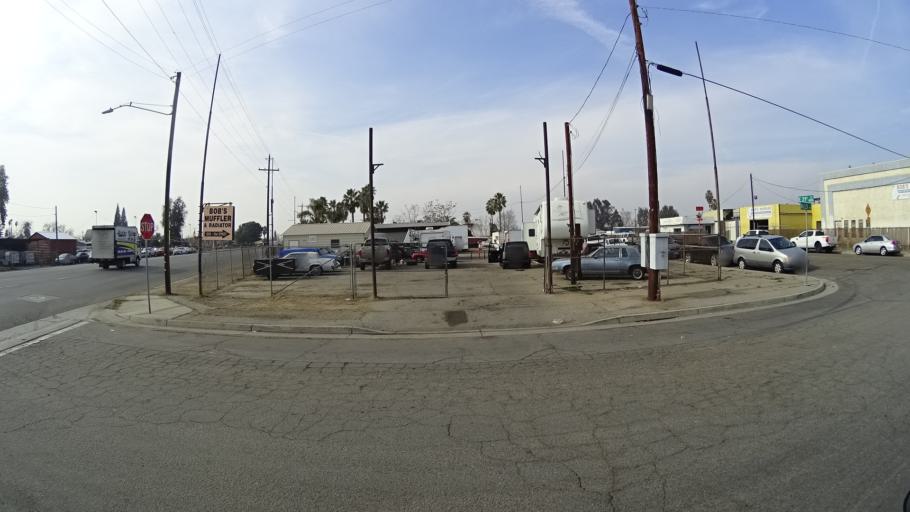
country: US
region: California
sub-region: Kern County
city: Bakersfield
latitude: 35.3734
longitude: -118.9840
